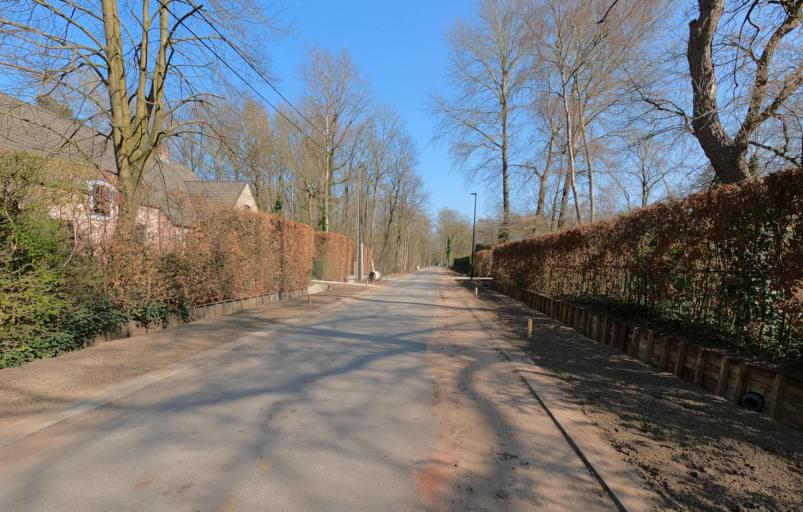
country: BE
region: Flanders
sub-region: Provincie Antwerpen
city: Schilde
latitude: 51.2672
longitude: 4.6045
